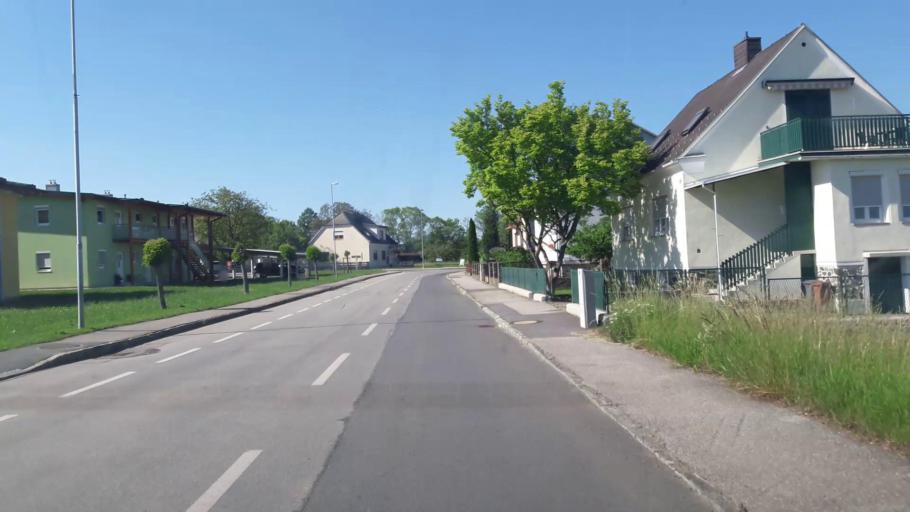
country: AT
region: Burgenland
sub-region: Politischer Bezirk Gussing
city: Ollersdorf im Burgenland
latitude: 47.1810
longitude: 16.1583
